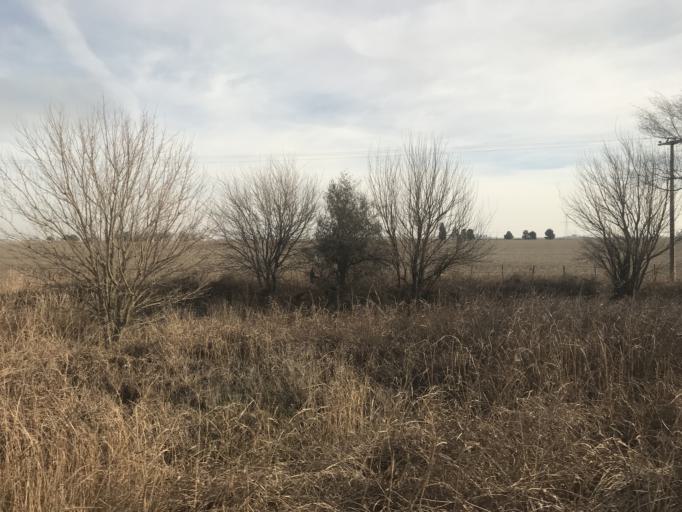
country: AR
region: Cordoba
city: Pilar
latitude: -31.7138
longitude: -63.8581
